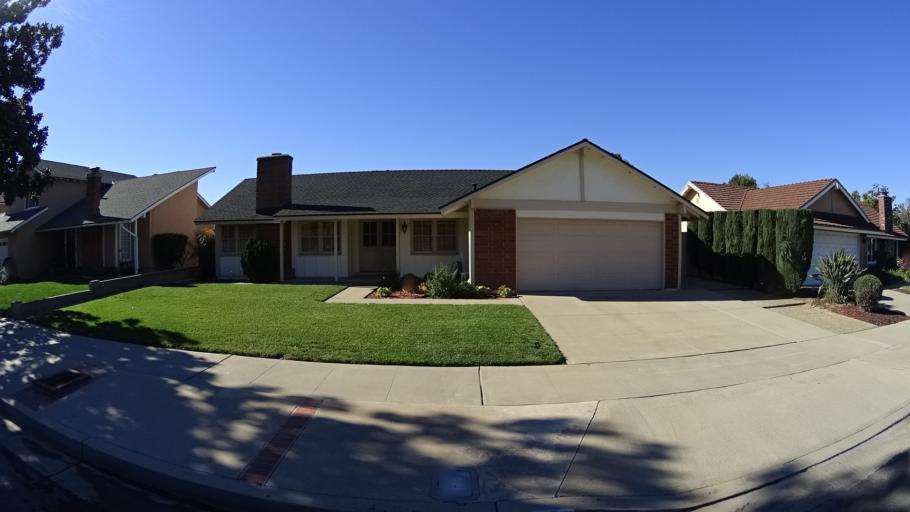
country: US
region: California
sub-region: Orange County
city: Placentia
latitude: 33.8413
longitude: -117.8480
